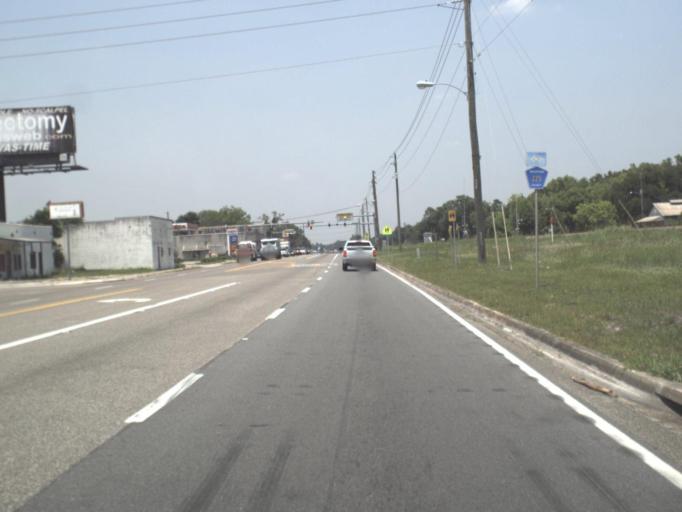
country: US
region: Florida
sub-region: Bradford County
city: Starke
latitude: 30.0426
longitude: -82.0724
